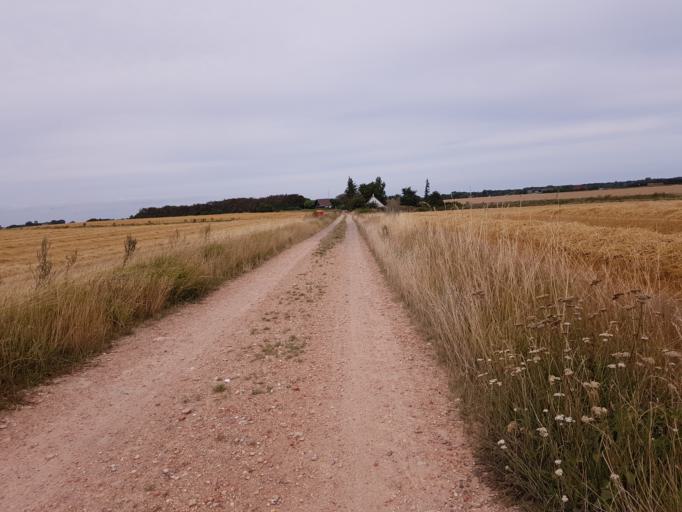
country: DK
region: Zealand
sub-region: Guldborgsund Kommune
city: Nykobing Falster
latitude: 54.5932
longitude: 11.9250
